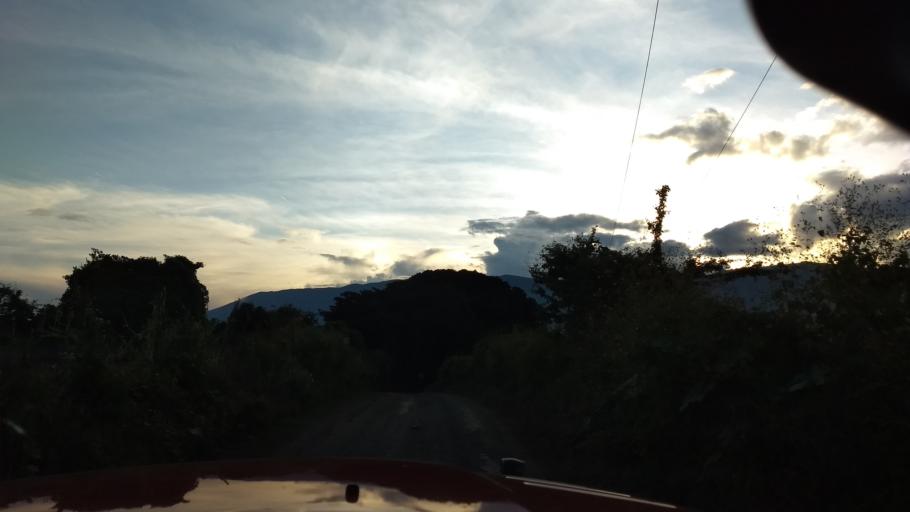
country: MX
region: Colima
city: Suchitlan
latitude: 19.4874
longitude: -103.7907
